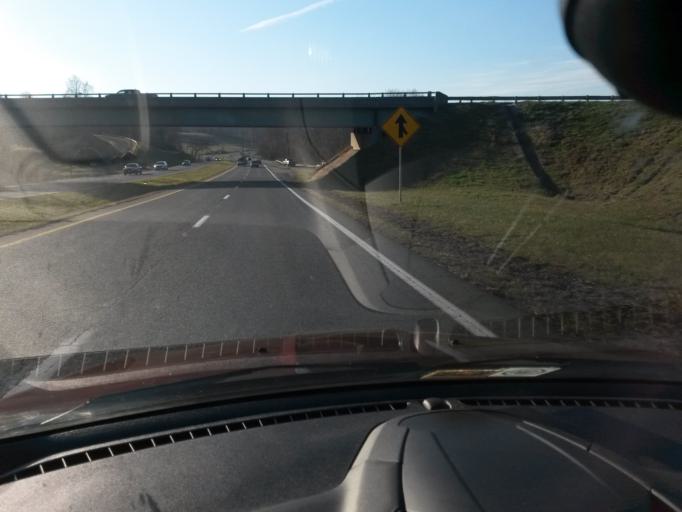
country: US
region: Virginia
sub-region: Amherst County
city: Madison Heights
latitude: 37.3861
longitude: -79.0622
